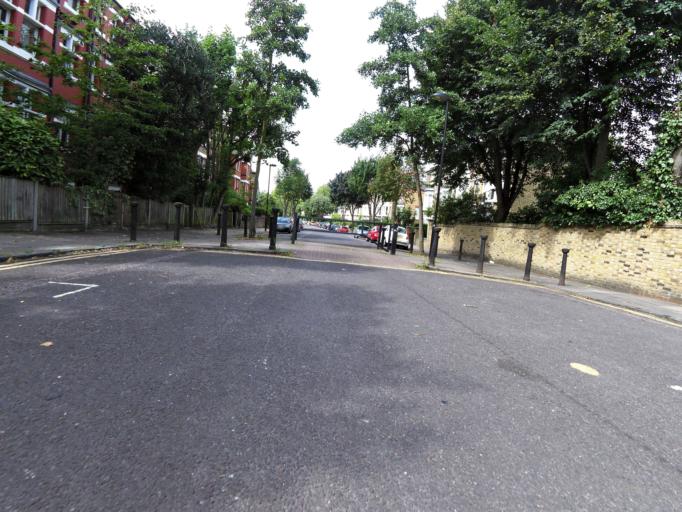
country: GB
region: England
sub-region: Greater London
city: Holloway
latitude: 51.5551
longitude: -0.1318
